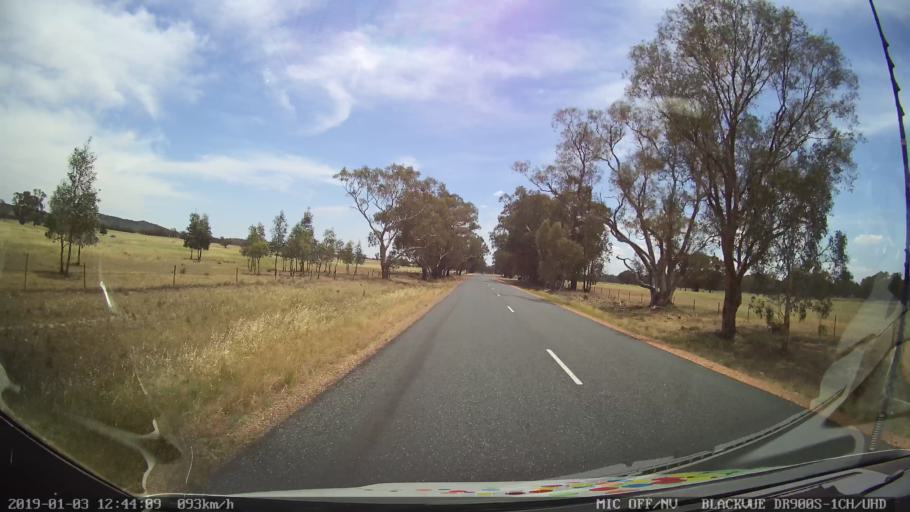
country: AU
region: New South Wales
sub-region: Weddin
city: Grenfell
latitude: -33.7653
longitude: 148.2149
